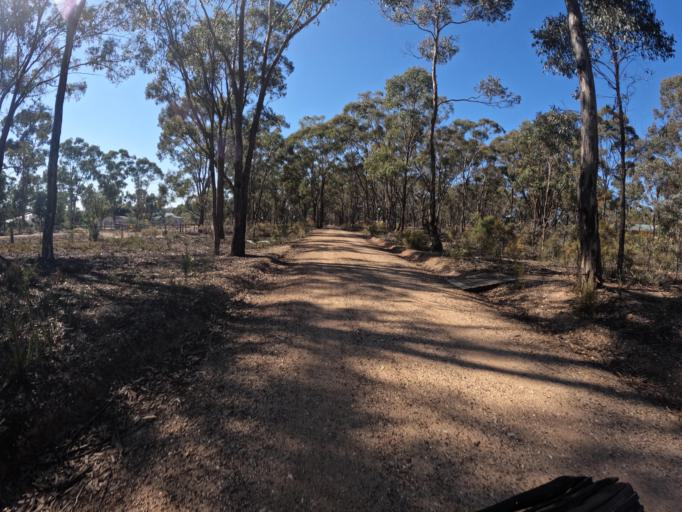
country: AU
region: Victoria
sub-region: Greater Bendigo
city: Kennington
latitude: -36.7809
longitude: 144.3857
